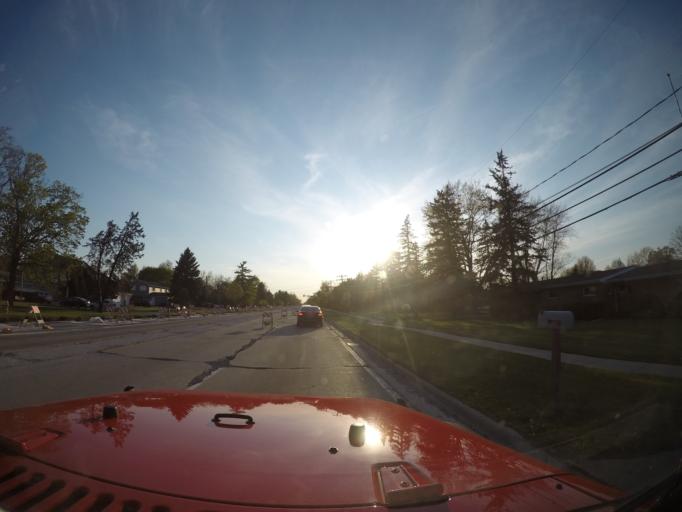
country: US
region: Illinois
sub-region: Cook County
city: Prospect Heights
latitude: 42.0878
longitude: -87.8961
